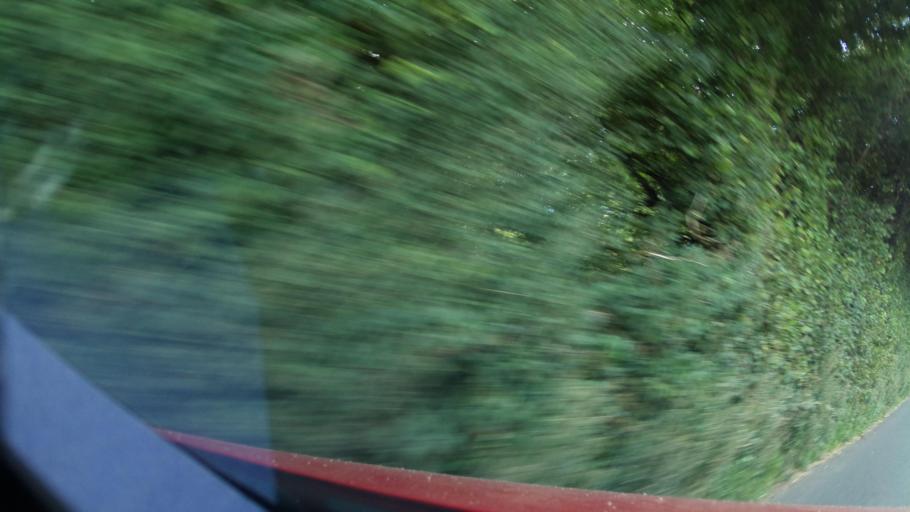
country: GB
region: England
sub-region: Devon
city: Tiverton
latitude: 50.8699
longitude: -3.4977
